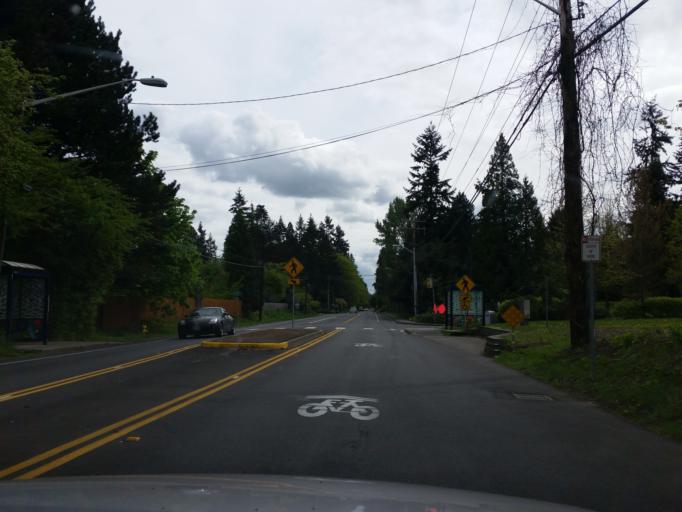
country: US
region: Washington
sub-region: King County
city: Kingsgate
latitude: 47.7047
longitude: -122.1645
